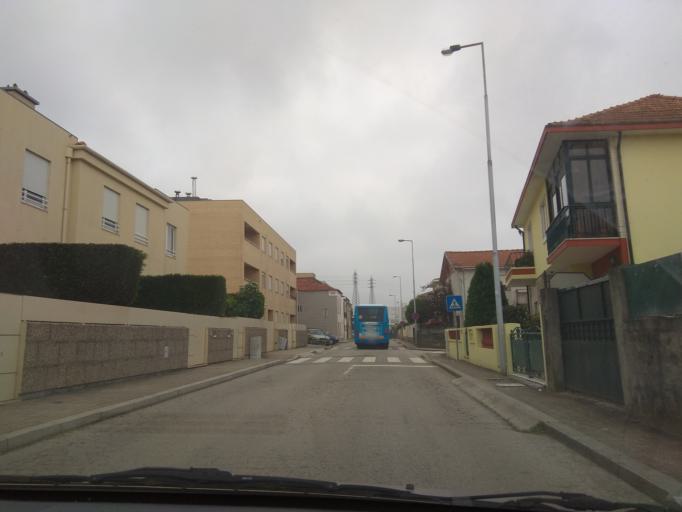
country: PT
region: Porto
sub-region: Matosinhos
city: Guifoes
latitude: 41.1932
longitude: -8.6605
